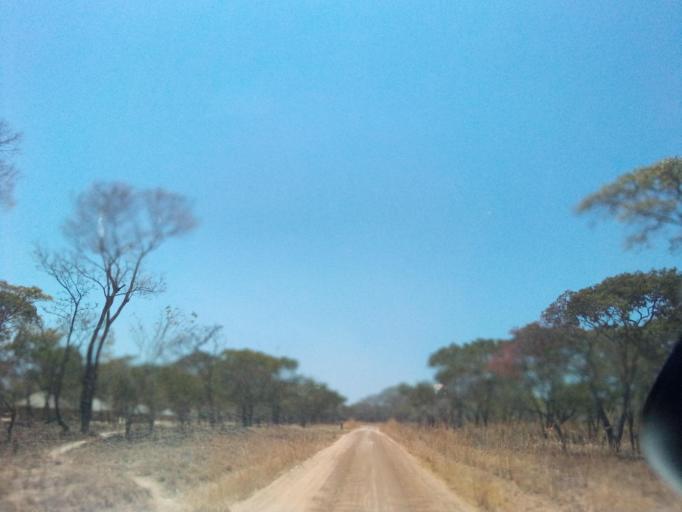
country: ZM
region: Northern
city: Mpika
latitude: -12.2537
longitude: 30.6931
